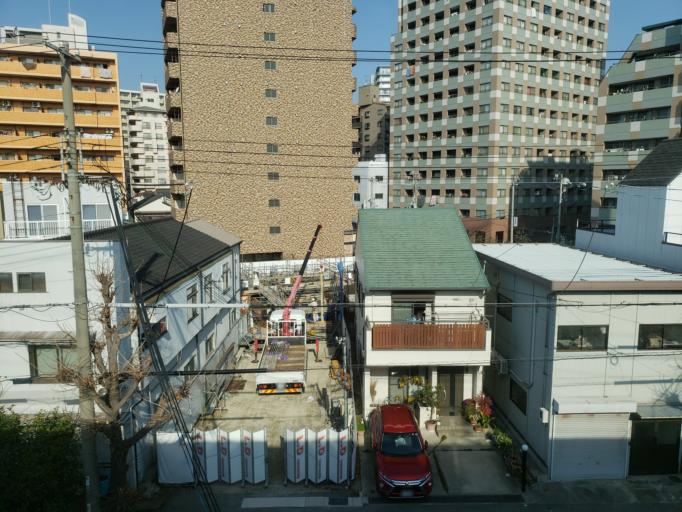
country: JP
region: Hyogo
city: Kobe
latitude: 34.6742
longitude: 135.1746
